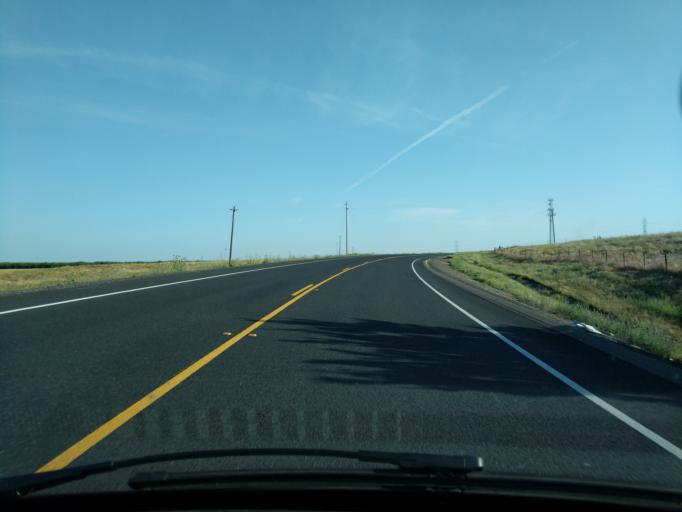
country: US
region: California
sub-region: San Joaquin County
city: Escalon
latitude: 37.9343
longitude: -120.9452
